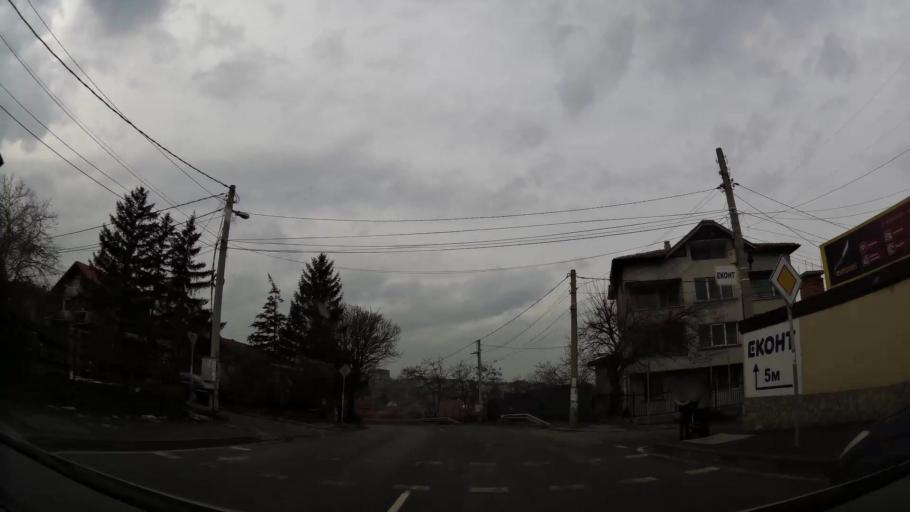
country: BG
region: Sofiya
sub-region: Obshtina Bozhurishte
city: Bozhurishte
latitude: 42.6967
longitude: 23.2257
